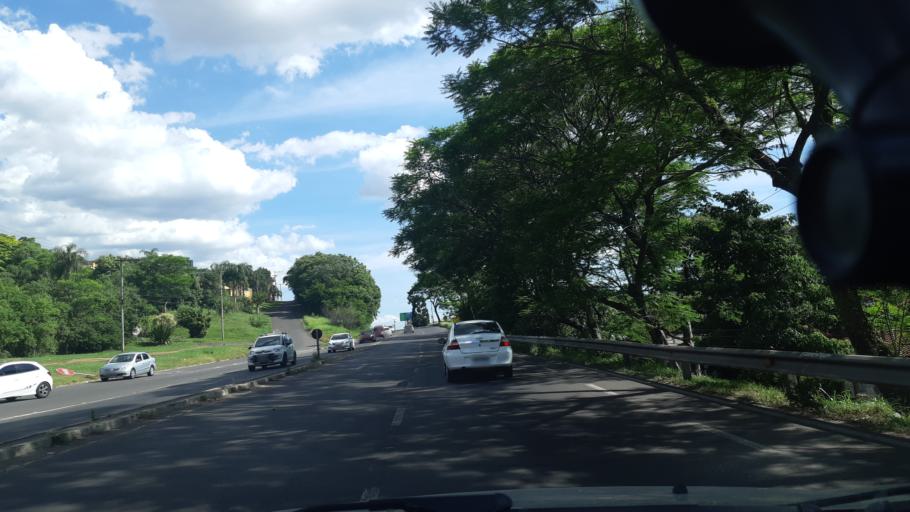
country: BR
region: Rio Grande do Sul
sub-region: Estancia Velha
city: Estancia Velha
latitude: -29.6507
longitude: -51.1445
